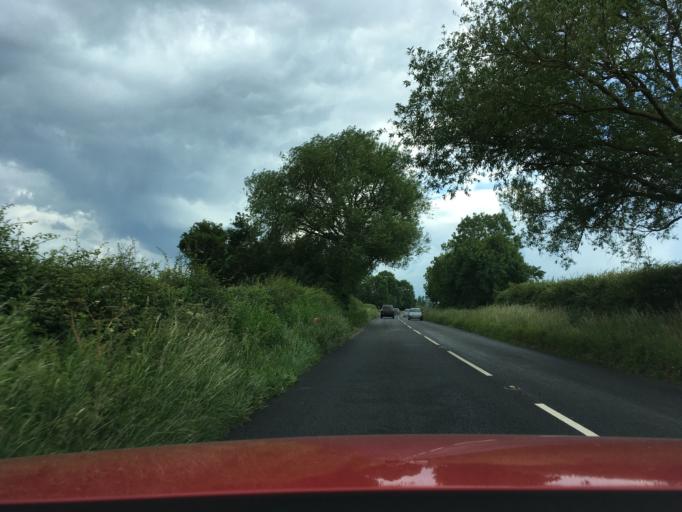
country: GB
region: England
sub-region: Gloucestershire
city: Stonehouse
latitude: 51.7874
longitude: -2.2895
